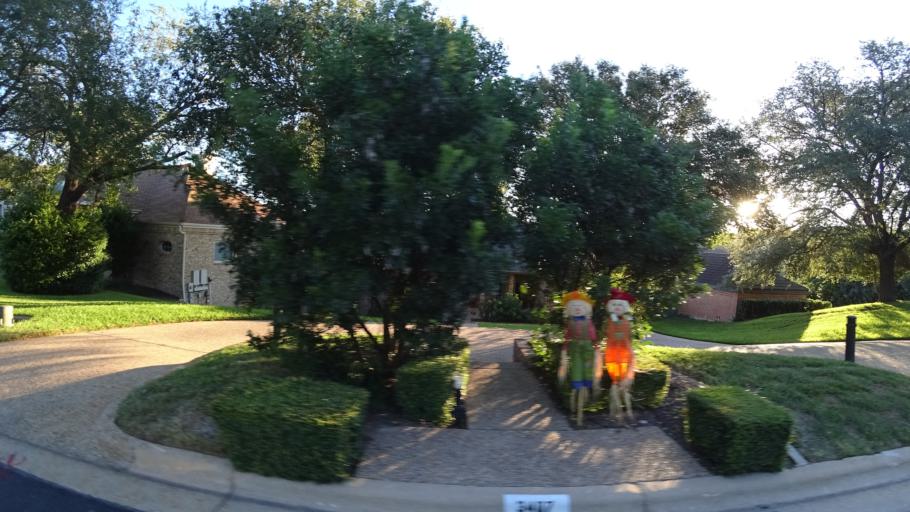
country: US
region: Texas
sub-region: Travis County
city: West Lake Hills
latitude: 30.3316
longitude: -97.8069
